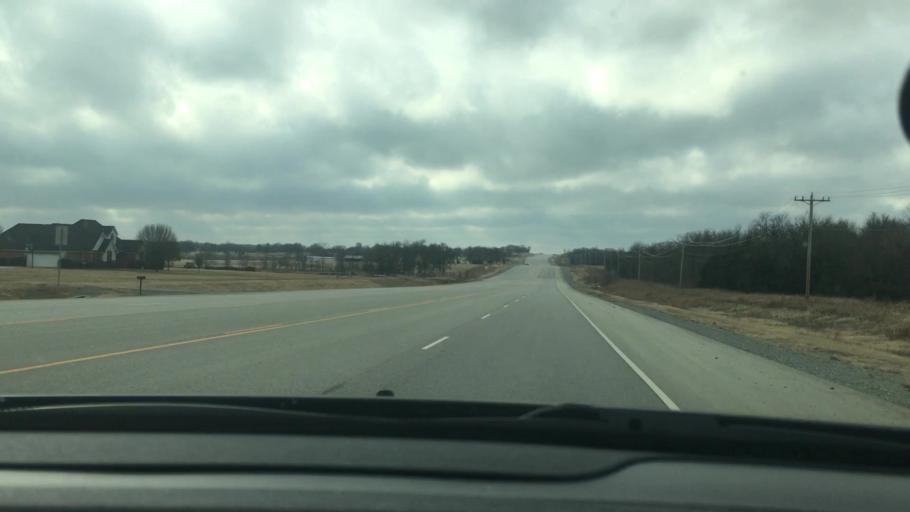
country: US
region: Oklahoma
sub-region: Bryan County
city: Durant
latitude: 34.0697
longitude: -96.3730
